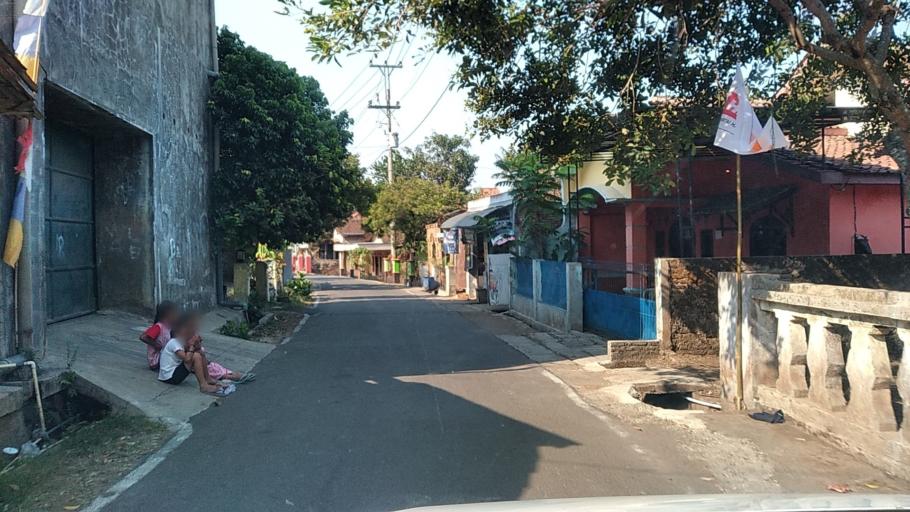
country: ID
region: Central Java
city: Semarang
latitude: -7.0313
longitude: 110.3428
